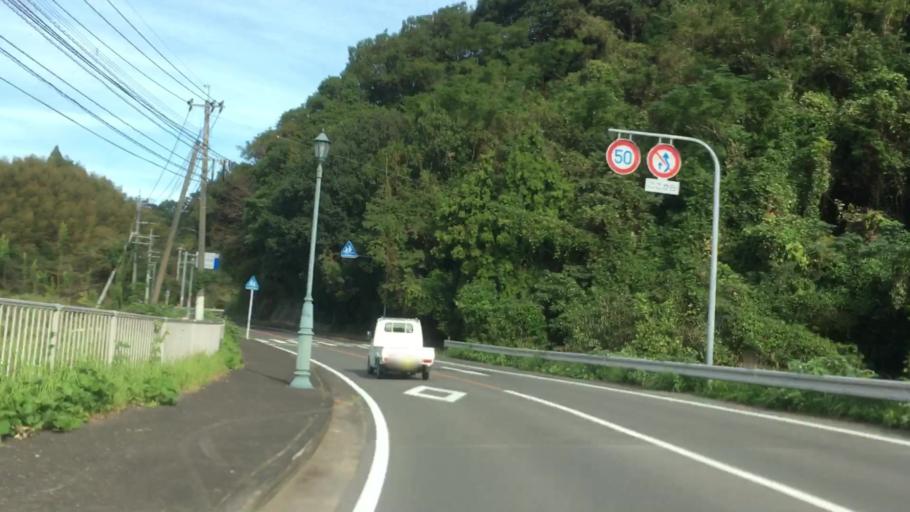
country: JP
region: Nagasaki
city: Sasebo
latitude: 33.0246
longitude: 129.6545
